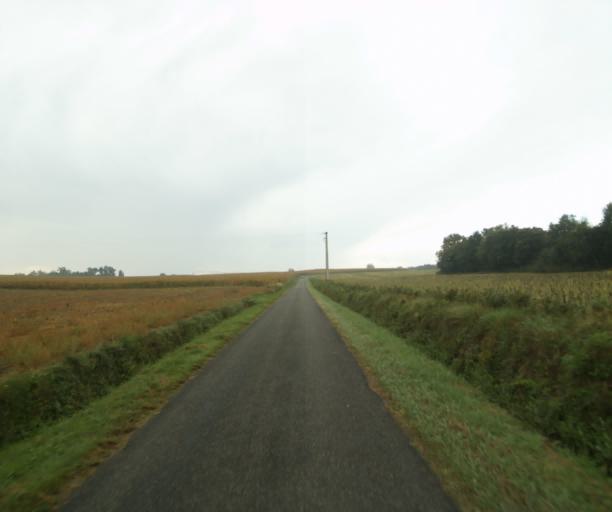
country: FR
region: Midi-Pyrenees
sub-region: Departement du Gers
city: Cazaubon
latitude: 43.9254
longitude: -0.0894
